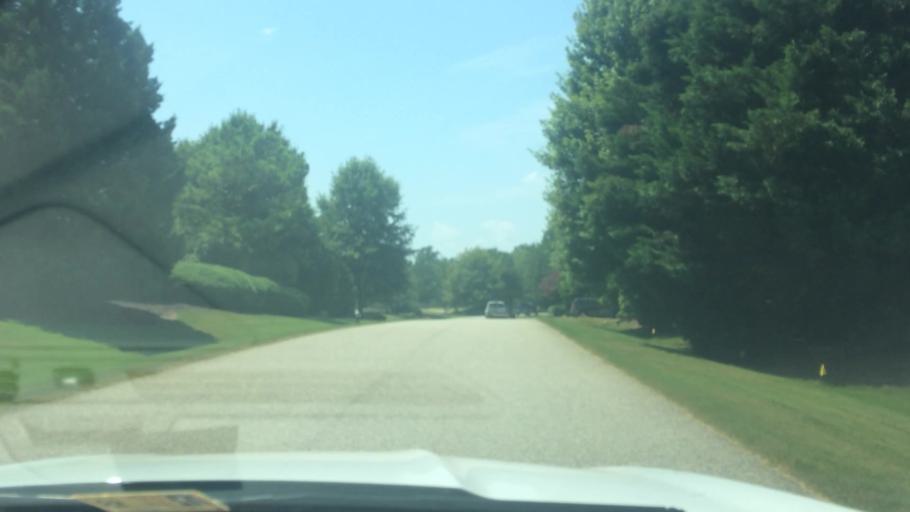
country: US
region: Virginia
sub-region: City of Williamsburg
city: Williamsburg
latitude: 37.2235
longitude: -76.6570
